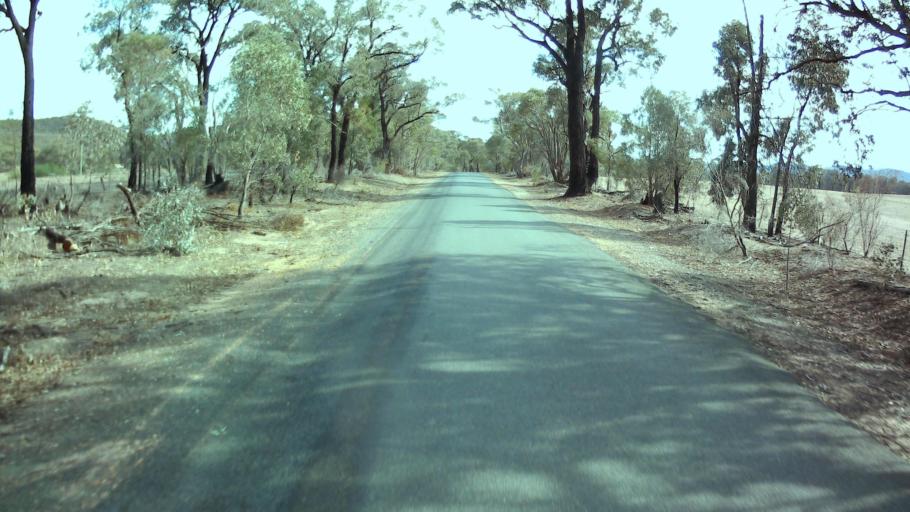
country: AU
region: New South Wales
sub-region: Weddin
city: Grenfell
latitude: -33.8748
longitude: 148.2016
